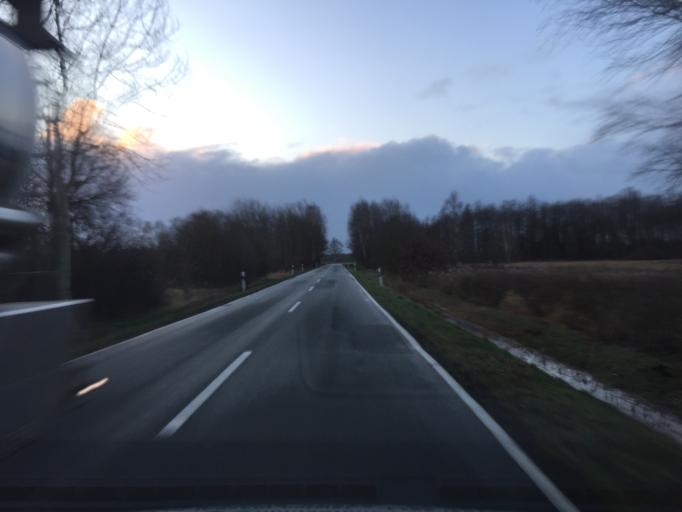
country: DE
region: Lower Saxony
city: Maasen
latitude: 52.6392
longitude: 8.8893
